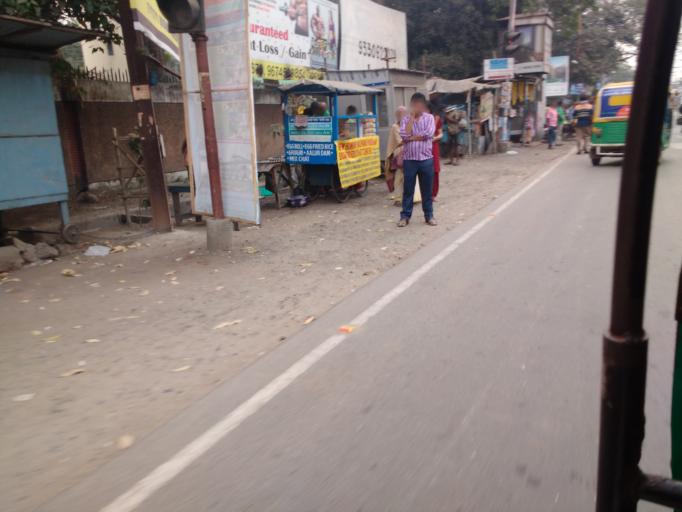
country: IN
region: West Bengal
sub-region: North 24 Parganas
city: Baranagar
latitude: 22.6456
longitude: 88.3776
